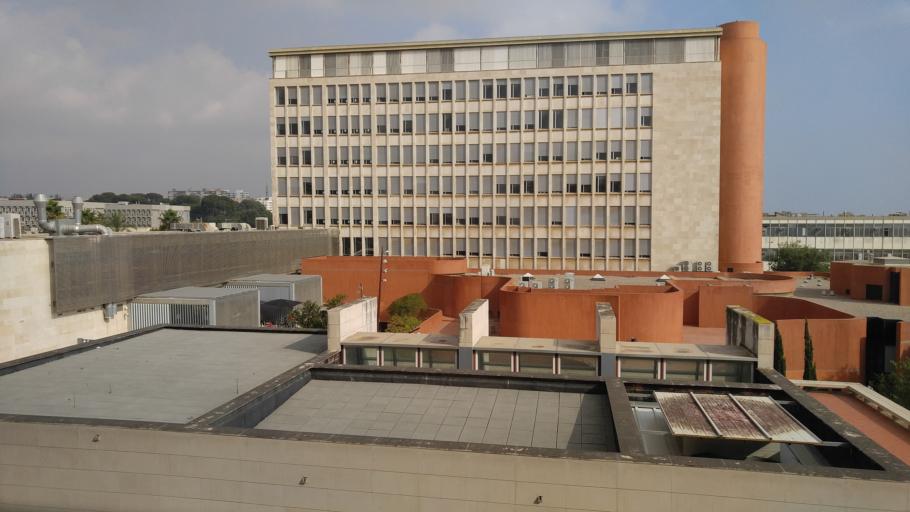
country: ES
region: Catalonia
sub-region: Provincia de Barcelona
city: les Corts
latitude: 41.3840
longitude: 2.1139
